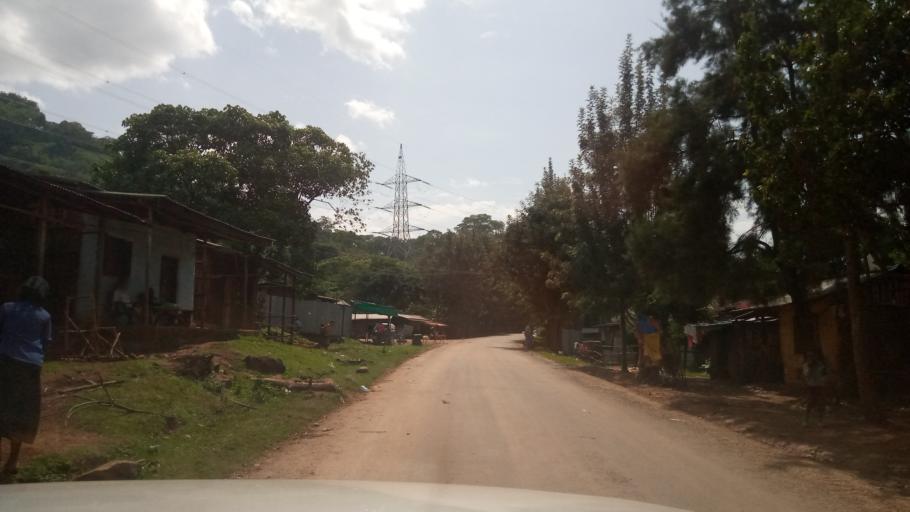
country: ET
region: Oromiya
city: Agaro
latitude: 7.9217
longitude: 36.5180
